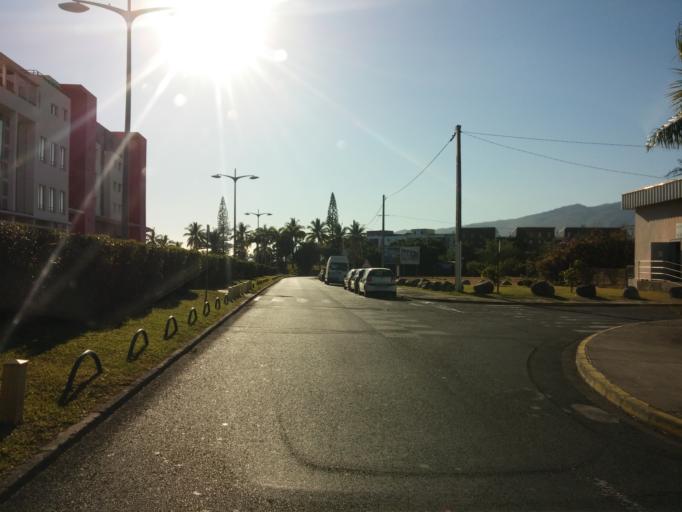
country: RE
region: Reunion
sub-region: Reunion
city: Le Port
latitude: -20.9321
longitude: 55.2956
